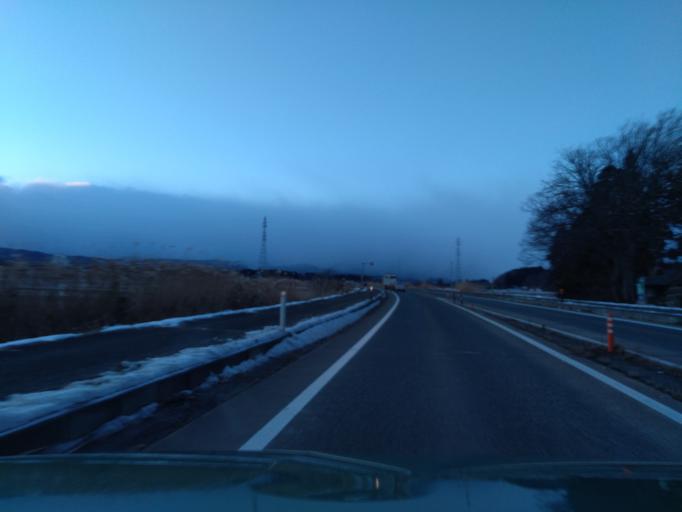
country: JP
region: Iwate
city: Shizukuishi
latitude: 39.6999
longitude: 140.9761
